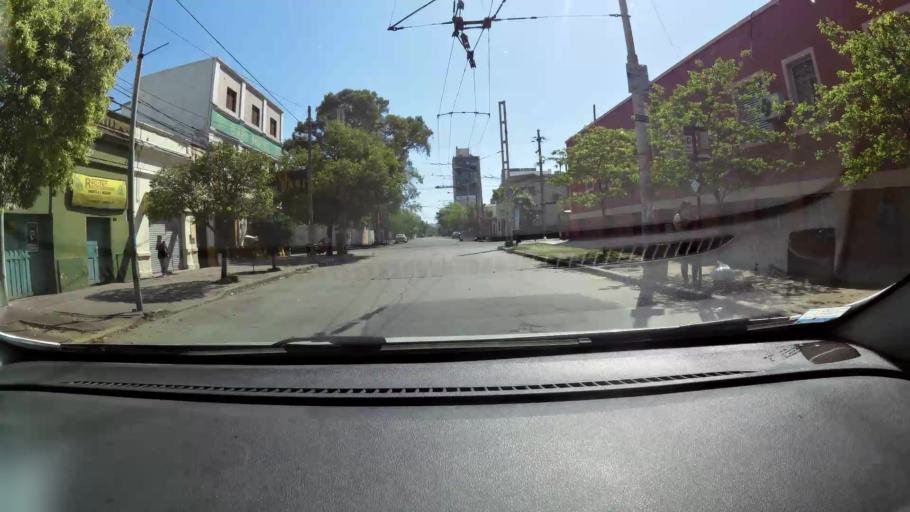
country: AR
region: Cordoba
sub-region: Departamento de Capital
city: Cordoba
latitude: -31.4098
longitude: -64.1644
